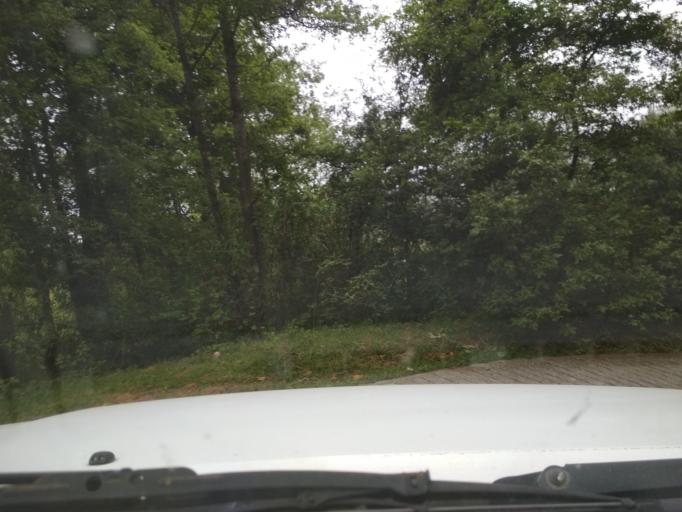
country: MX
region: Veracruz
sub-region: La Perla
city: Chilapa
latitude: 18.9744
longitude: -97.1969
